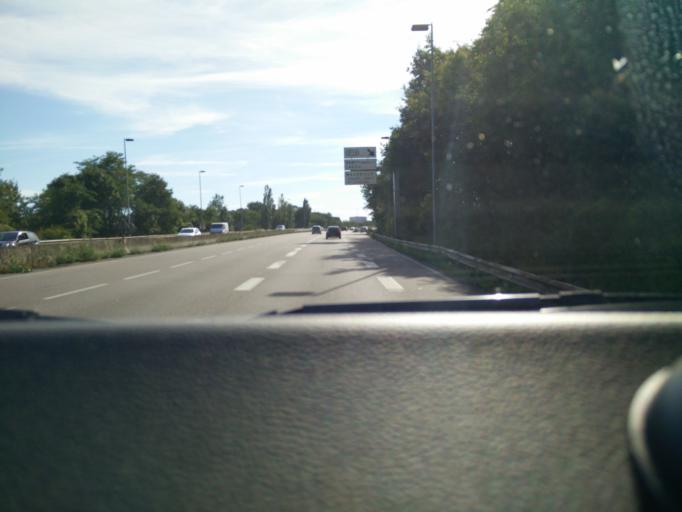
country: FR
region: Lorraine
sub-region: Departement de Meurthe-et-Moselle
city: Laxou
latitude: 48.7074
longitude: 6.1408
